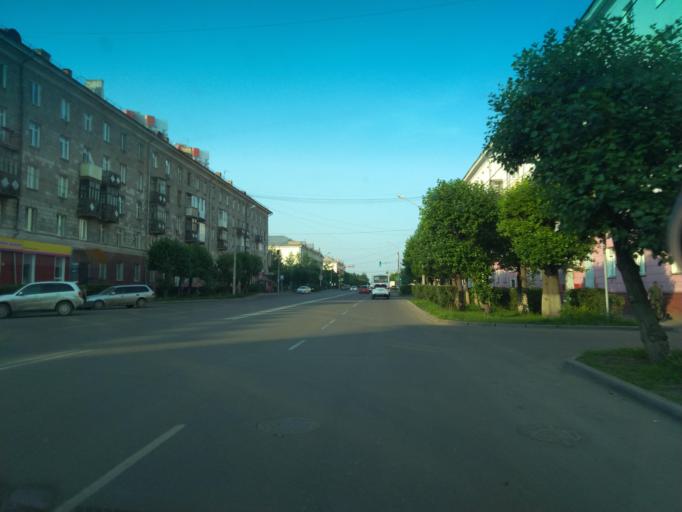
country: RU
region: Krasnoyarskiy
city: Krasnoyarsk
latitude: 55.9981
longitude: 92.9310
